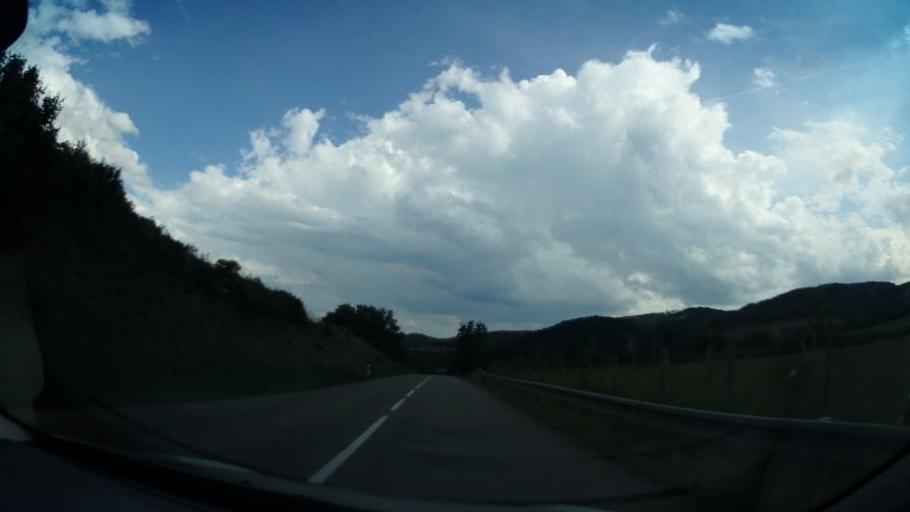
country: CZ
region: South Moravian
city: Predklasteri
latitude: 49.3627
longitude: 16.3848
